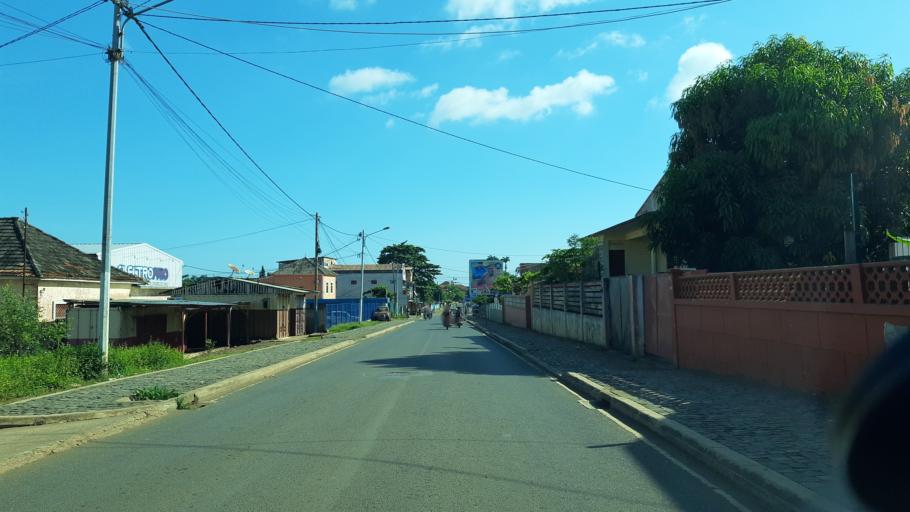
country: ST
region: Sao Tome Island
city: Sao Tome
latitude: 0.3325
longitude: 6.7305
